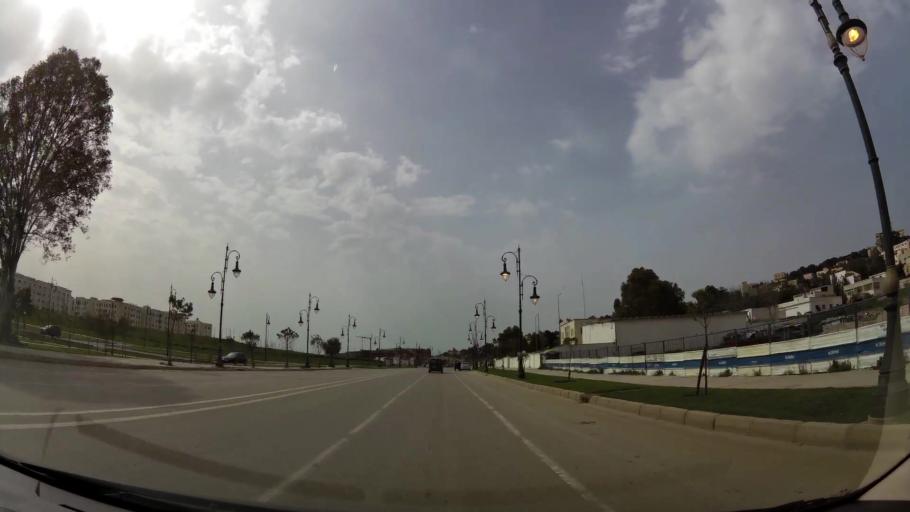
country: MA
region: Tanger-Tetouan
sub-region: Tanger-Assilah
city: Boukhalef
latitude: 35.7433
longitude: -5.8824
